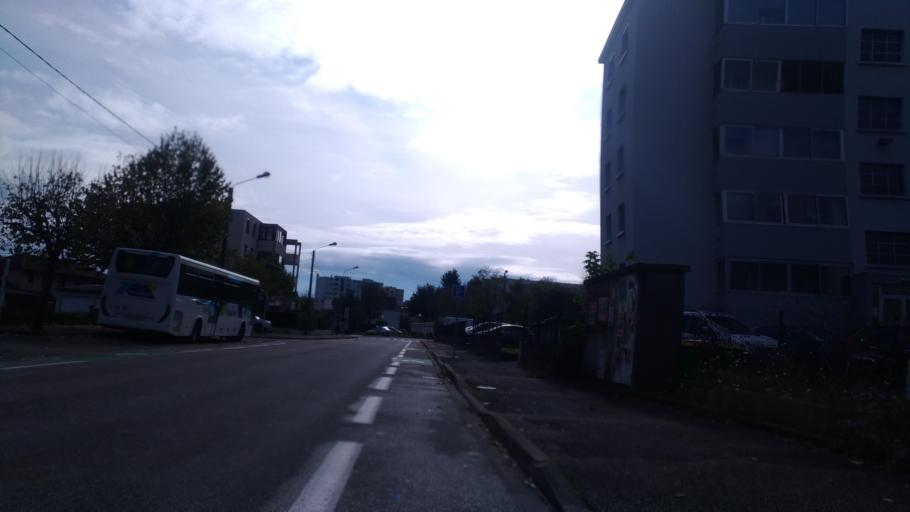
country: FR
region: Rhone-Alpes
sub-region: Departement de l'Isere
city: Fontaine
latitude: 45.1946
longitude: 5.6830
